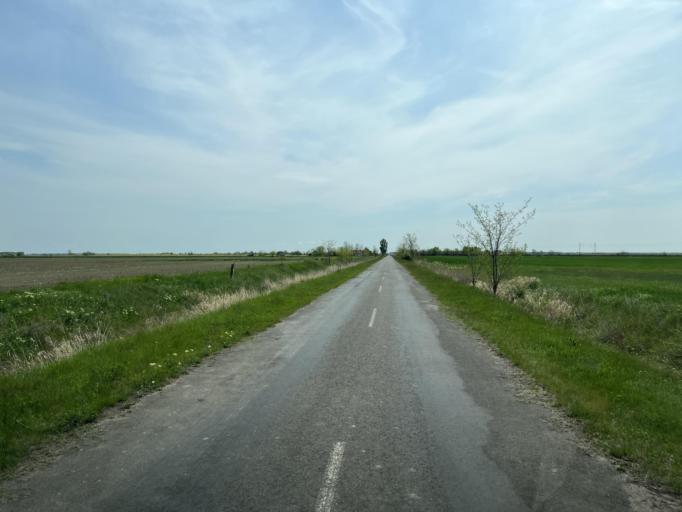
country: HU
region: Pest
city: Tapiogyorgye
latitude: 47.3239
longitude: 19.9627
